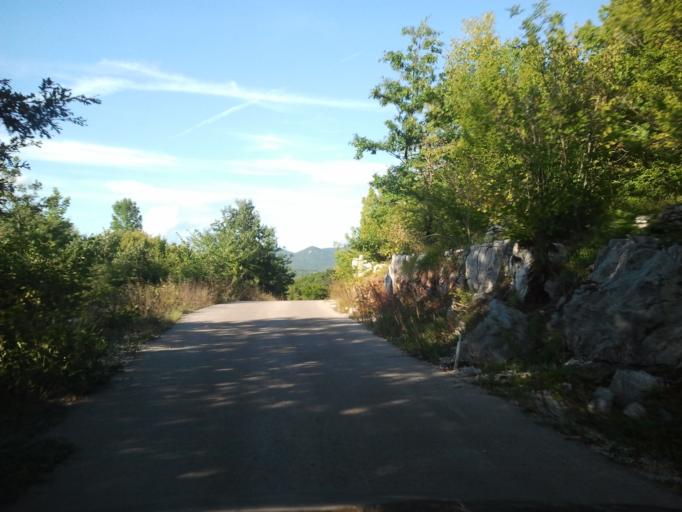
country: HR
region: Zadarska
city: Gracac
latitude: 44.3674
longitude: 15.7039
